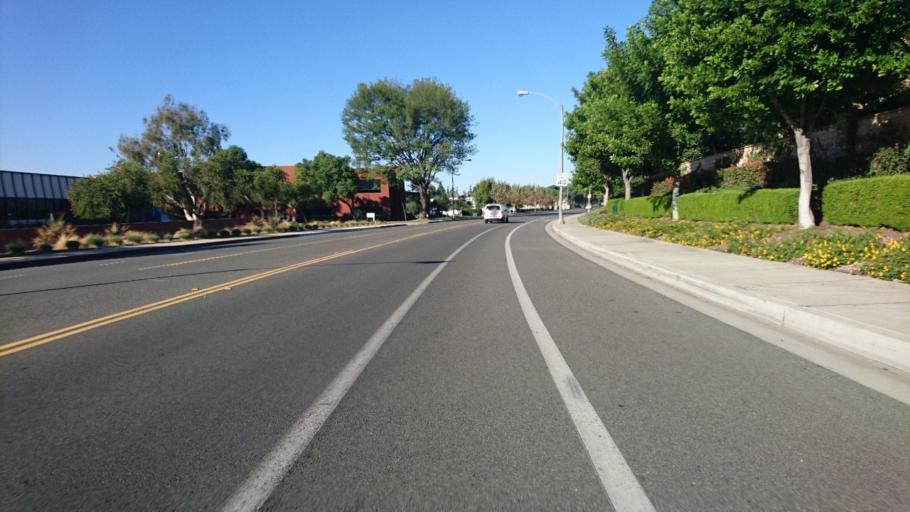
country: US
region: California
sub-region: Los Angeles County
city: La Verne
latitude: 34.0963
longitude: -117.7493
